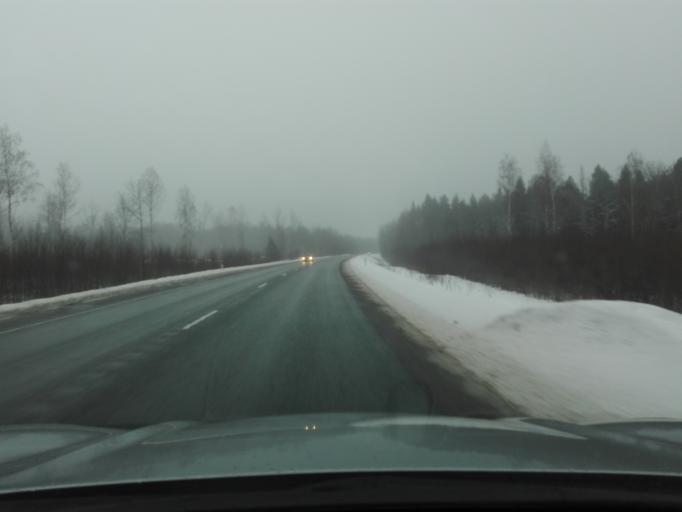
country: EE
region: Raplamaa
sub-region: Kohila vald
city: Kohila
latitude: 59.1368
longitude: 24.7918
